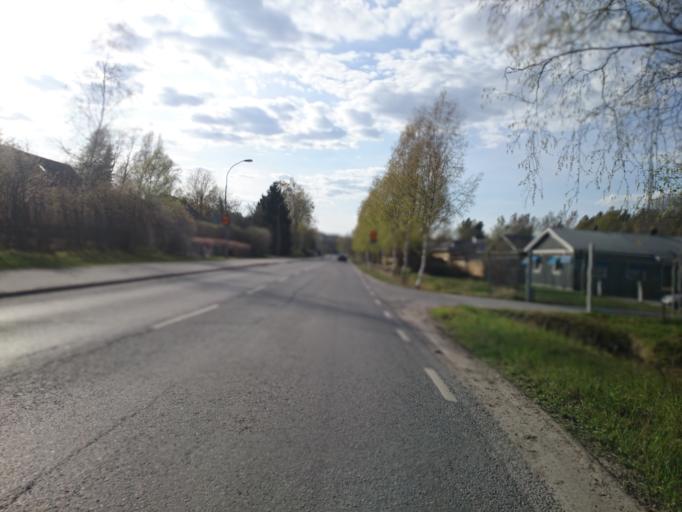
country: SE
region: Stockholm
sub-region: Huddinge Kommun
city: Huddinge
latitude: 59.2483
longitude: 17.9689
